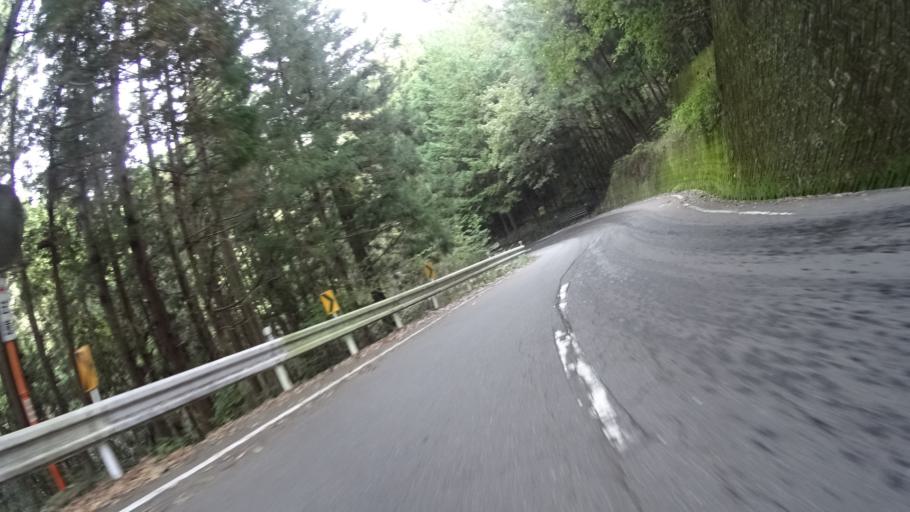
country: JP
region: Yamanashi
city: Otsuki
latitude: 35.6236
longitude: 139.0212
